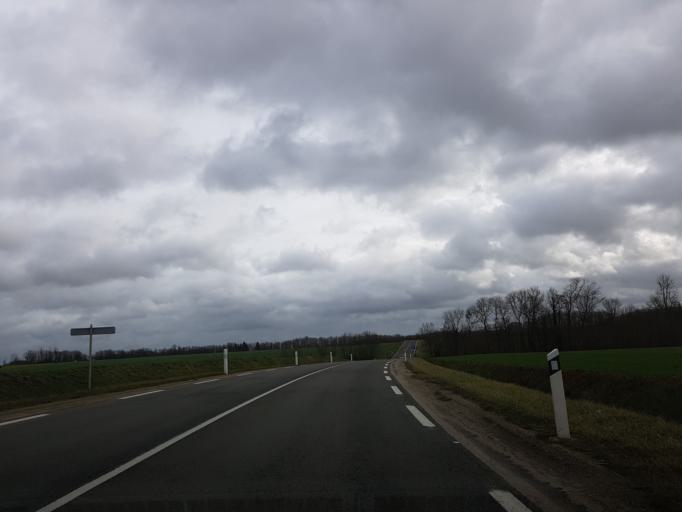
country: FR
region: Champagne-Ardenne
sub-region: Departement de la Haute-Marne
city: Chalindrey
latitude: 47.8428
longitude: 5.4633
